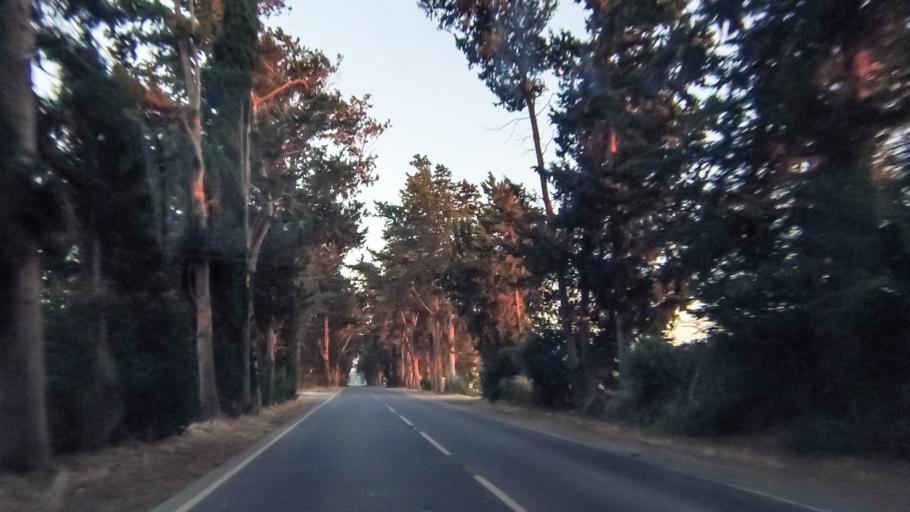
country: CY
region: Larnaka
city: Kolossi
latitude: 34.6406
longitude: 32.9454
